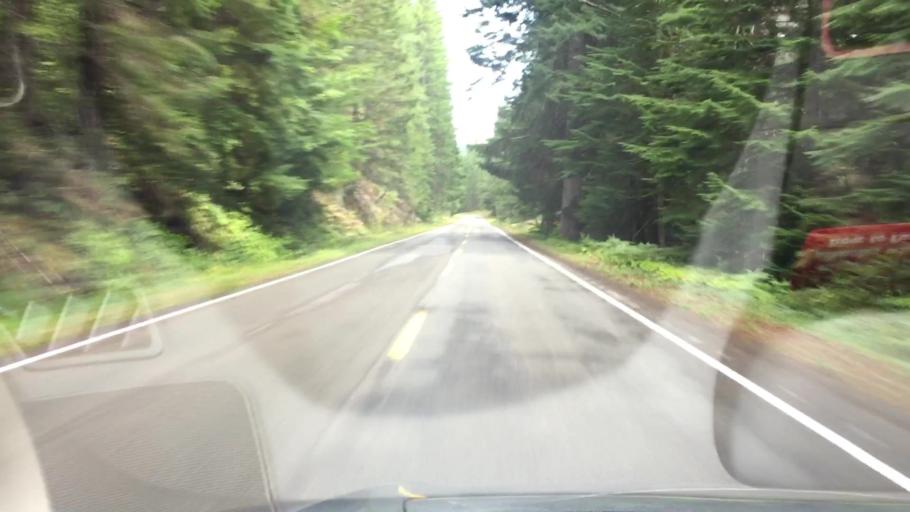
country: US
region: Washington
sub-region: Pierce County
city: Buckley
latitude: 46.7579
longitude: -121.6261
